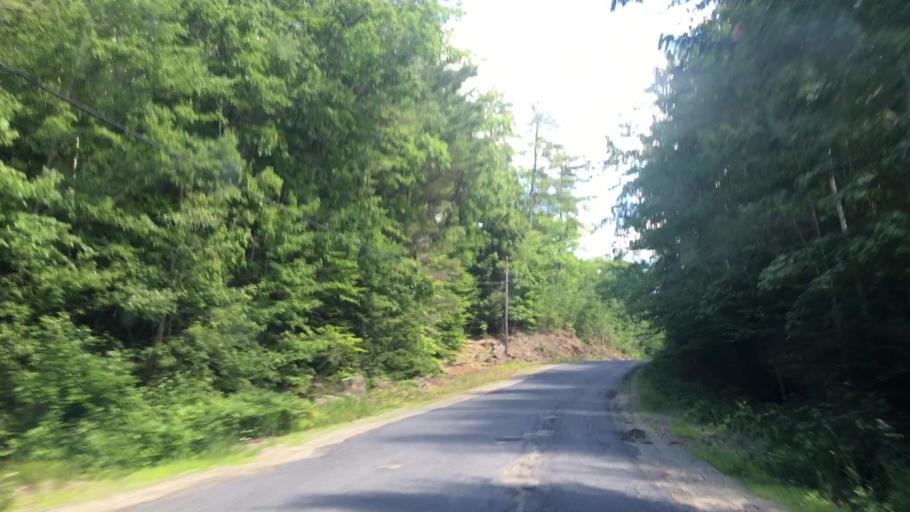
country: US
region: Maine
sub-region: Franklin County
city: Chesterville
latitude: 44.5604
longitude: -70.1292
